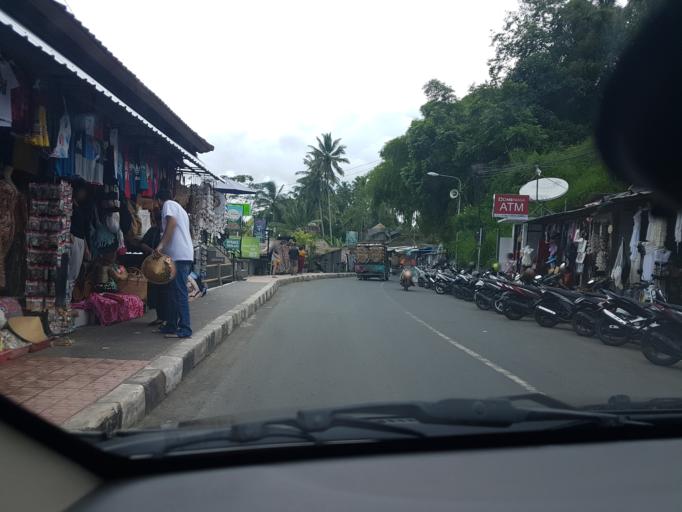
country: ID
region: Bali
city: Tegalalang
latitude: -8.4331
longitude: 115.2786
